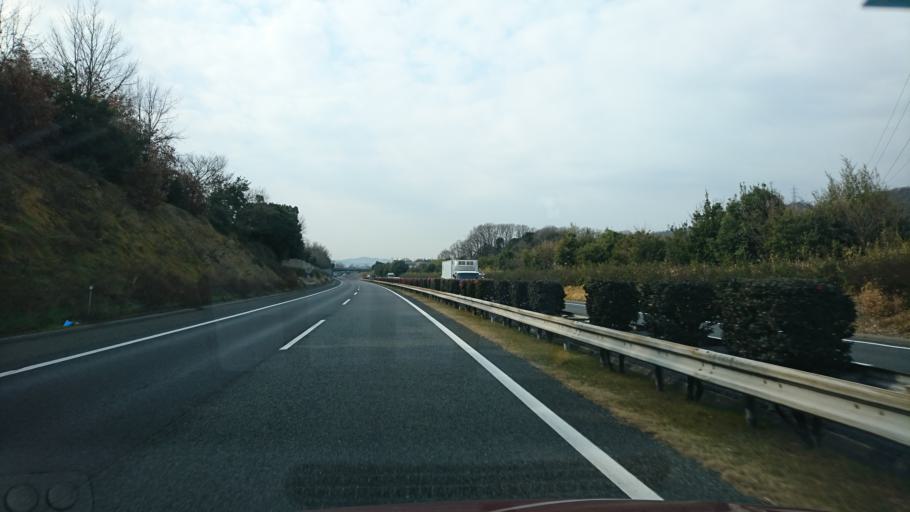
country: JP
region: Hiroshima
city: Kannabecho-yahiro
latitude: 34.5210
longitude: 133.4252
